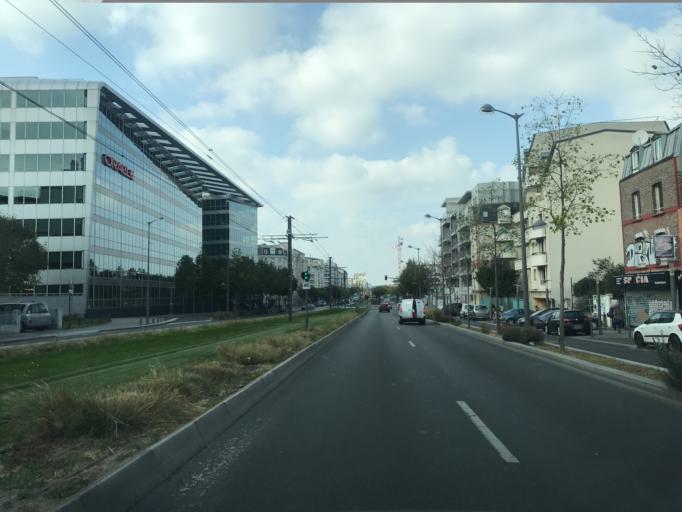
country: FR
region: Ile-de-France
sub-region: Departement des Hauts-de-Seine
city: La Garenne-Colombes
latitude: 48.9094
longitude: 2.2361
